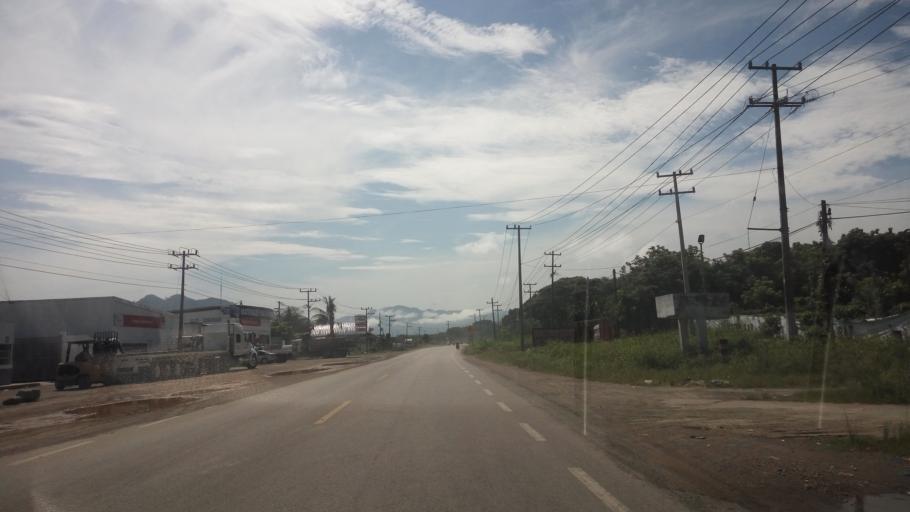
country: MX
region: Tabasco
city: Teapa
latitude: 17.5795
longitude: -92.9626
